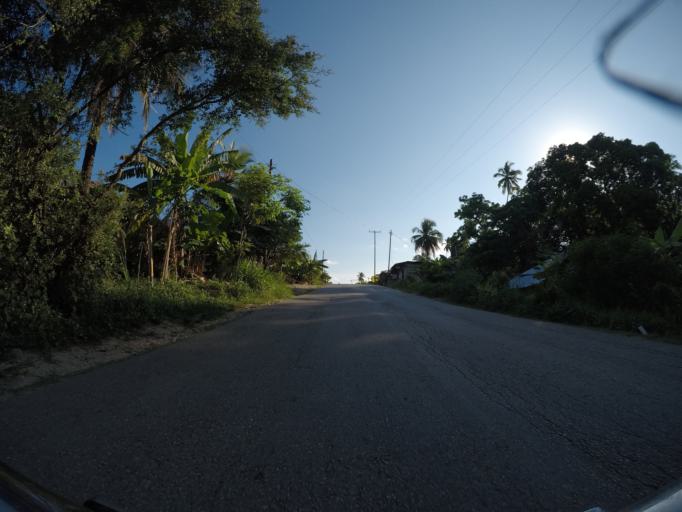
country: TZ
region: Pemba South
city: Chake Chake
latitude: -5.2919
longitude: 39.7605
